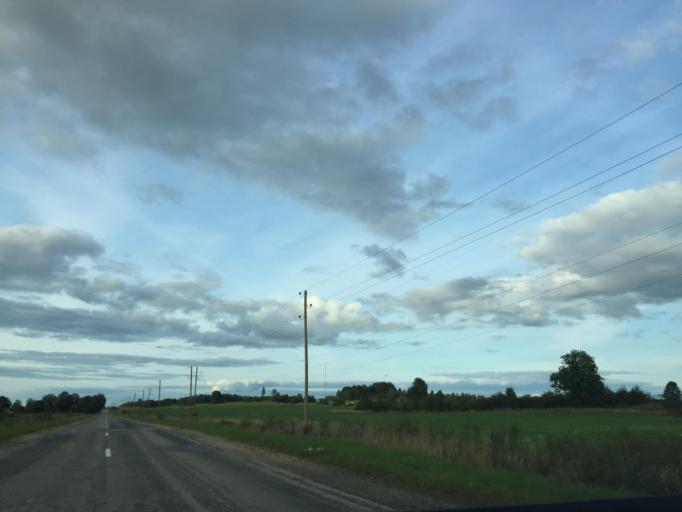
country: LV
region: Nereta
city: Nereta
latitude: 56.2200
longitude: 25.3177
